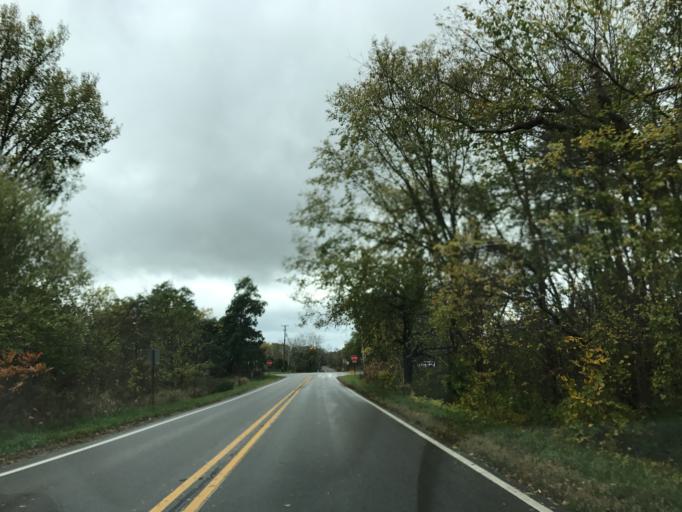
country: US
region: Michigan
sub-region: Oakland County
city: South Lyon
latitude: 42.3634
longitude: -83.6611
